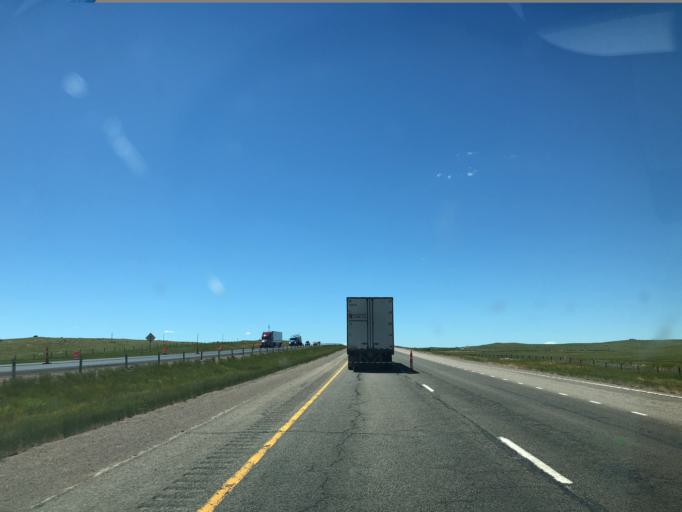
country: US
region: Wyoming
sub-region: Laramie County
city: Cheyenne
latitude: 41.0965
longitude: -105.1849
